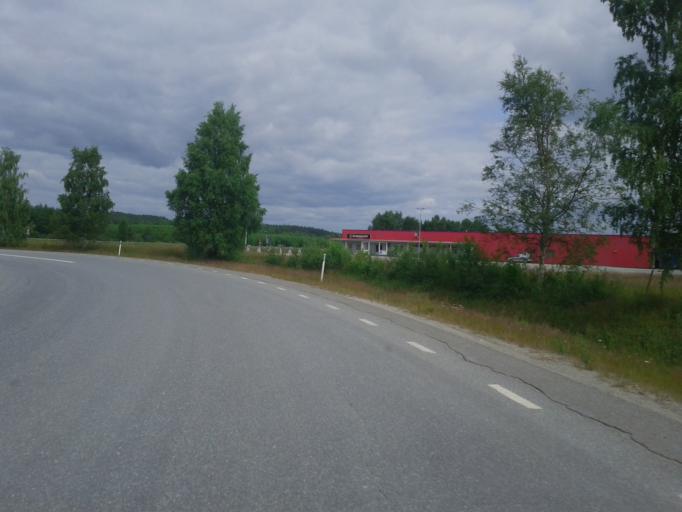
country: SE
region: Vaesternorrland
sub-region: OErnskoeldsviks Kommun
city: Bjasta
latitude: 63.2069
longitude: 18.4894
